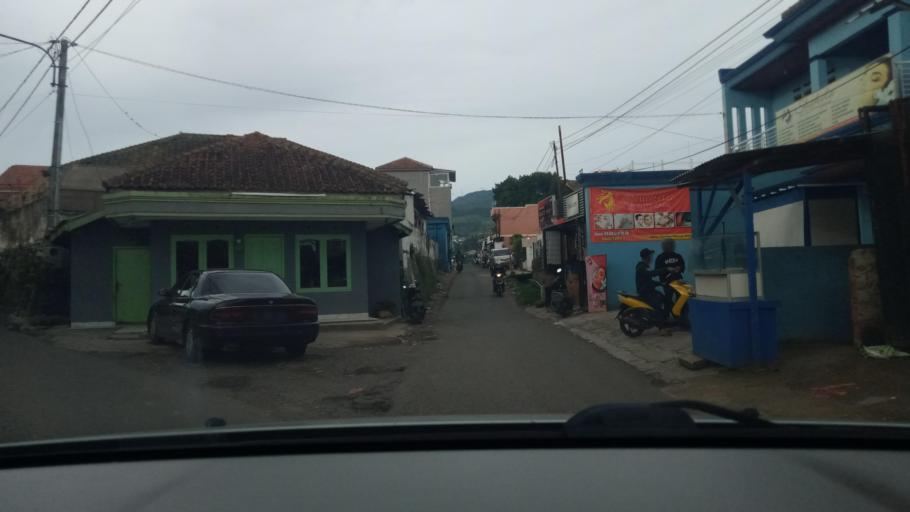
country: ID
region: West Java
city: Lembang
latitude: -6.8054
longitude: 107.5889
